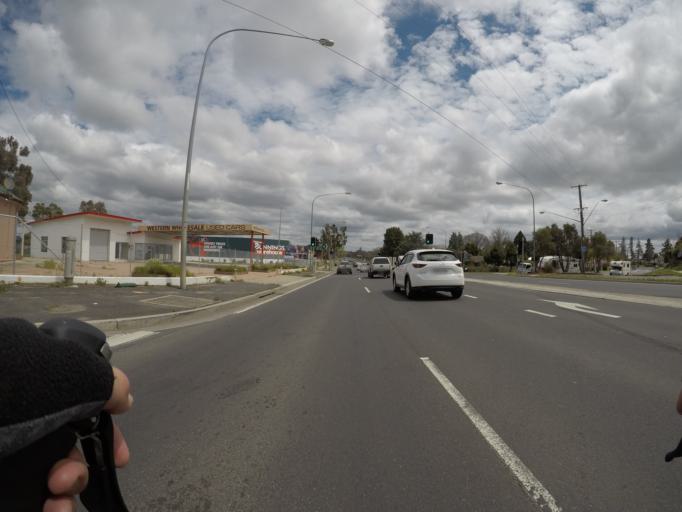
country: AU
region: New South Wales
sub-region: Bathurst Regional
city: Kelso
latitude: -33.4188
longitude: 149.6047
